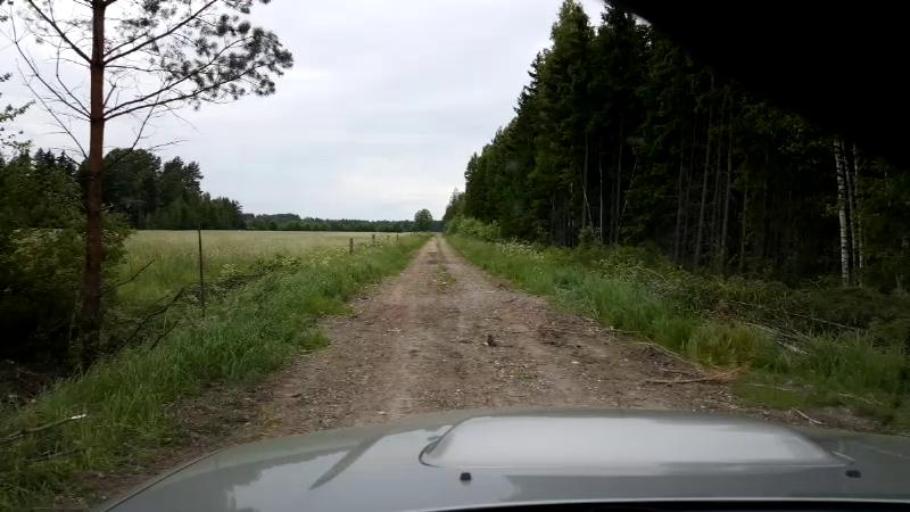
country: EE
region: Paernumaa
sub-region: Sindi linn
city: Sindi
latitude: 58.5108
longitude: 24.6354
